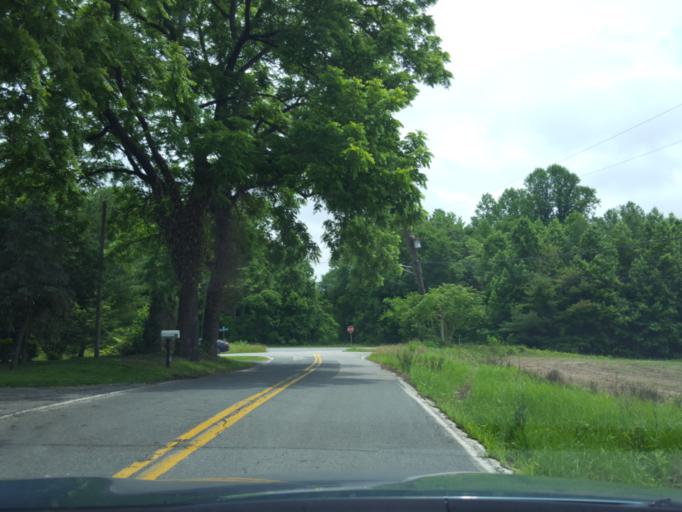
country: US
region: Maryland
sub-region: Calvert County
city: Dunkirk
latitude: 38.7814
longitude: -76.6654
